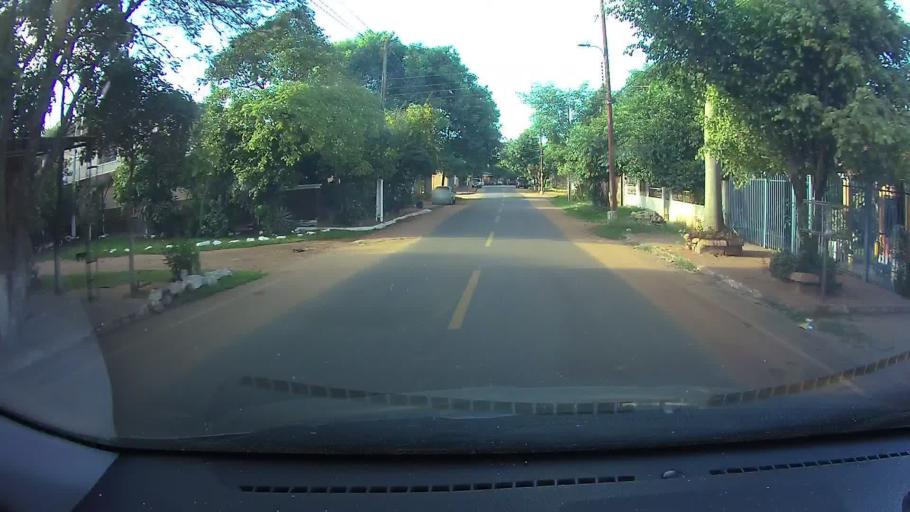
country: PY
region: Central
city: San Lorenzo
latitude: -25.2765
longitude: -57.4822
